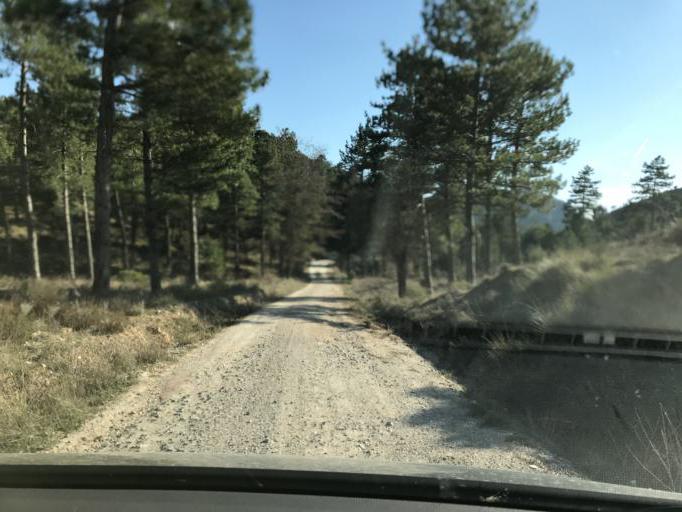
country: ES
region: Andalusia
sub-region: Provincia de Granada
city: Beas de Granada
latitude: 37.2407
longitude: -3.4454
